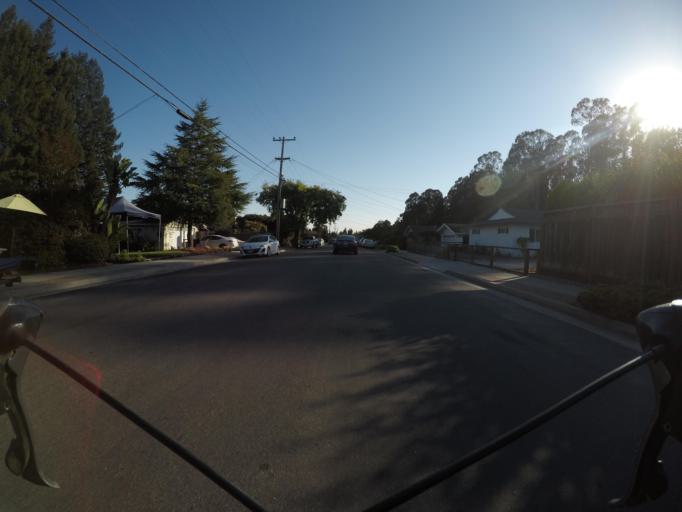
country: US
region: California
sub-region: Santa Cruz County
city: Live Oak
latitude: 36.9993
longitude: -121.9771
